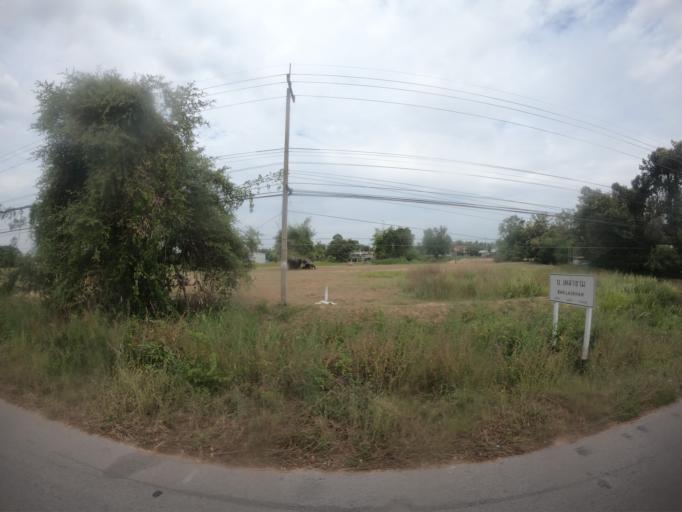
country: TH
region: Roi Et
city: Changhan
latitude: 16.0973
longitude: 103.5346
